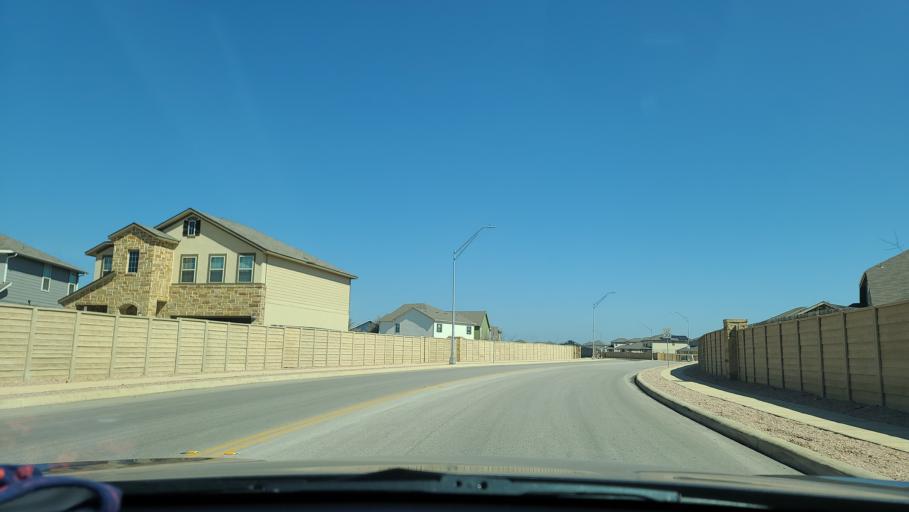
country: US
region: Texas
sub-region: Bexar County
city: Leon Valley
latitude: 29.5621
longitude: -98.6211
